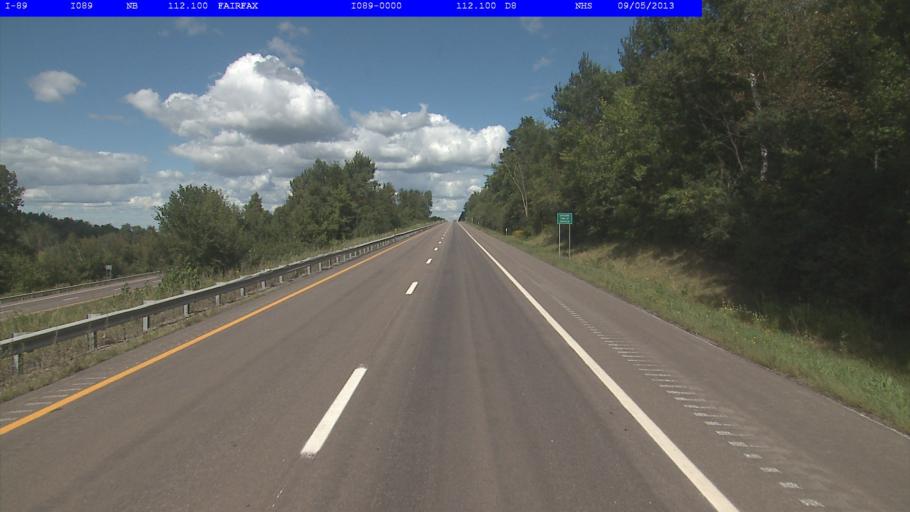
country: US
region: Vermont
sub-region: Franklin County
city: Saint Albans
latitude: 44.7713
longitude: -73.0750
